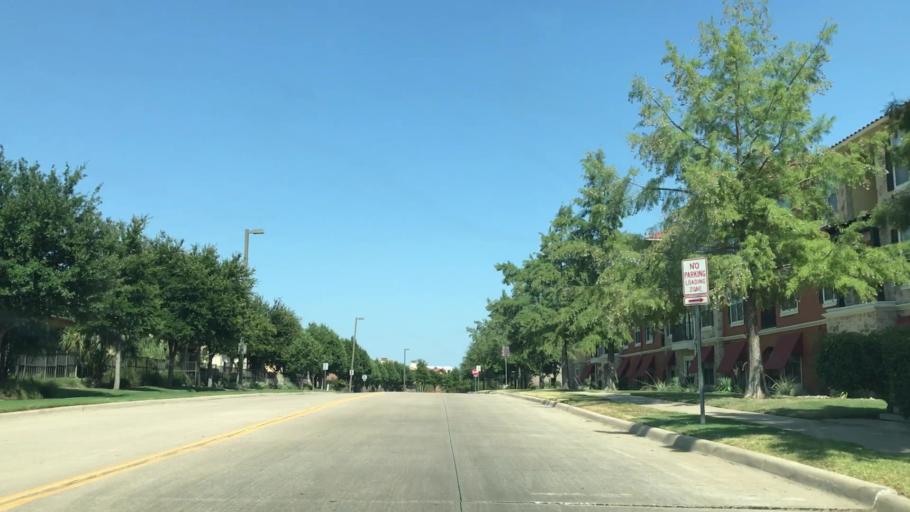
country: US
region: Texas
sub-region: Dallas County
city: Farmers Branch
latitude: 32.8979
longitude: -96.9567
